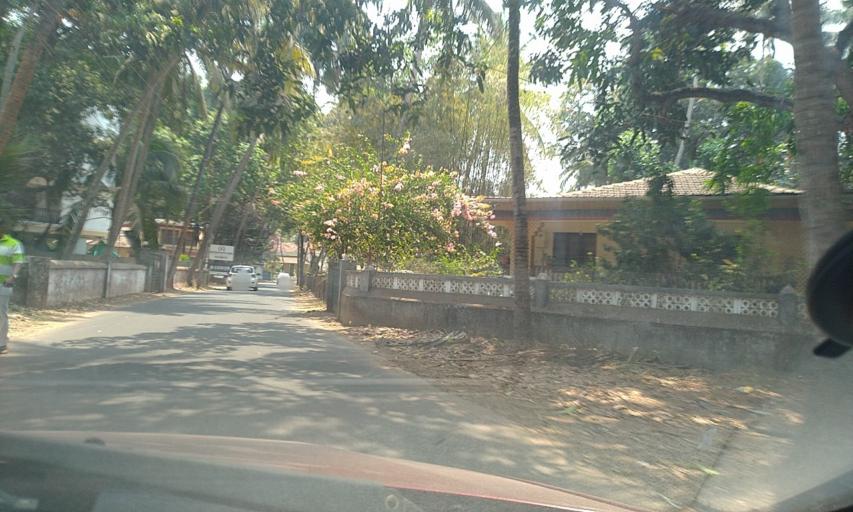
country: IN
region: Goa
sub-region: North Goa
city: Saligao
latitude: 15.5527
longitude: 73.7810
